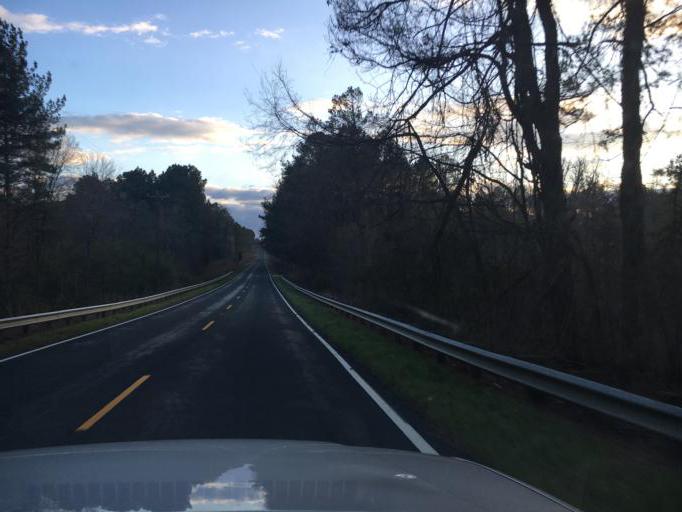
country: US
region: South Carolina
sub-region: Greenwood County
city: Greenwood
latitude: 34.0627
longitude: -82.2316
